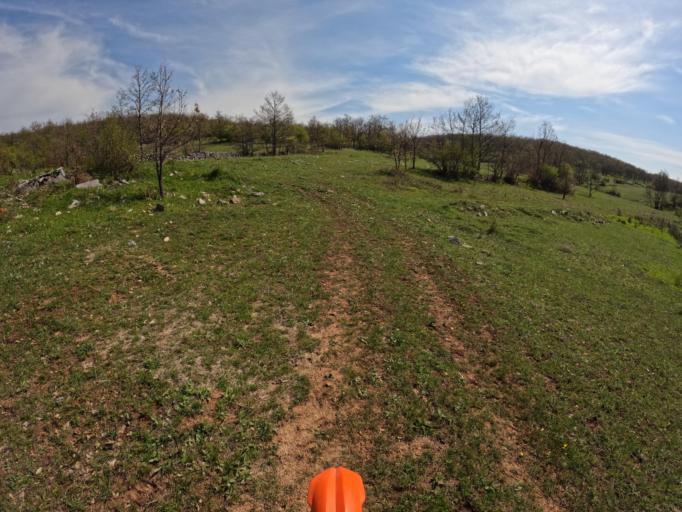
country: BA
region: Federation of Bosnia and Herzegovina
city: Orasac
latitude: 44.4386
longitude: 16.0984
